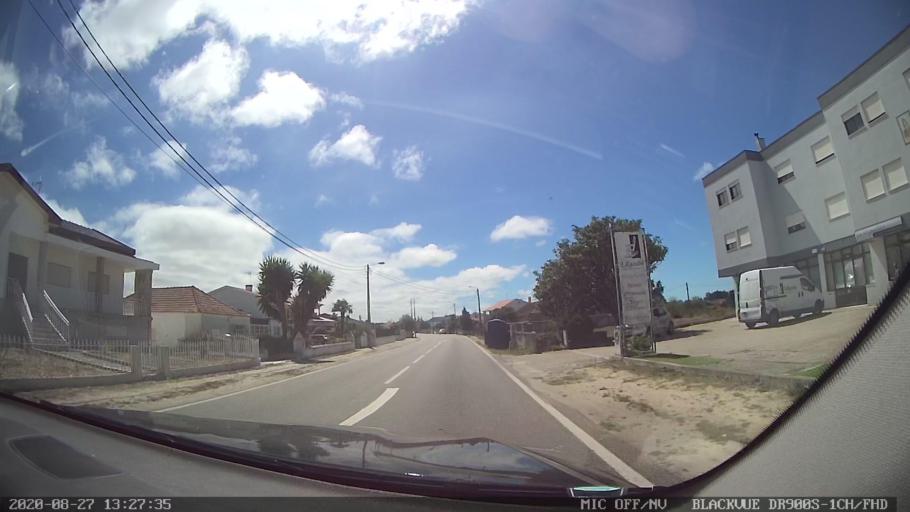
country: PT
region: Aveiro
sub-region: Vagos
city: Vagos
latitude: 40.5292
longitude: -8.6789
